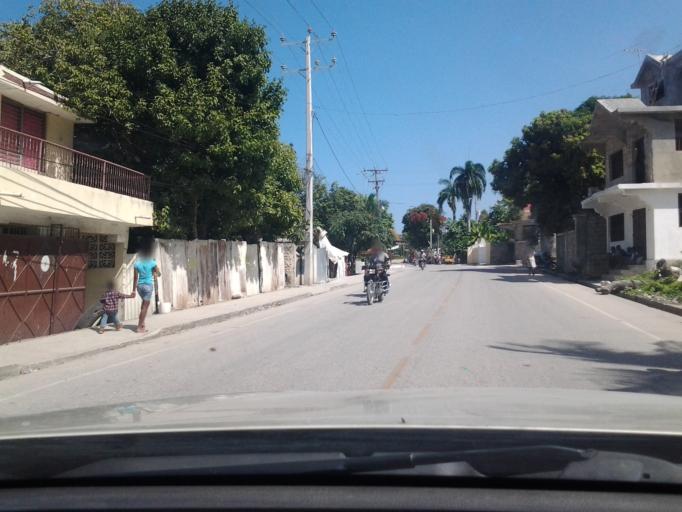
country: HT
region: Ouest
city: Tigwav
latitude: 18.4388
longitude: -72.8525
